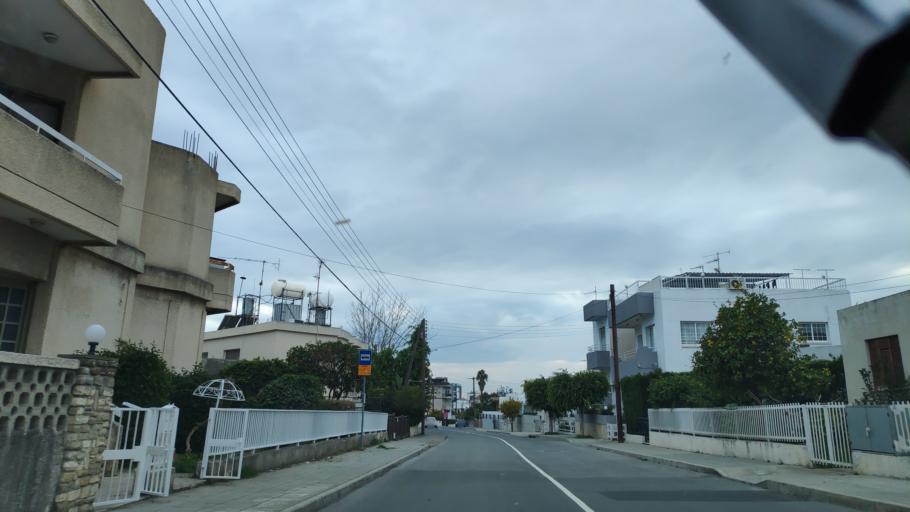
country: CY
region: Limassol
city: Limassol
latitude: 34.6953
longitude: 33.0231
